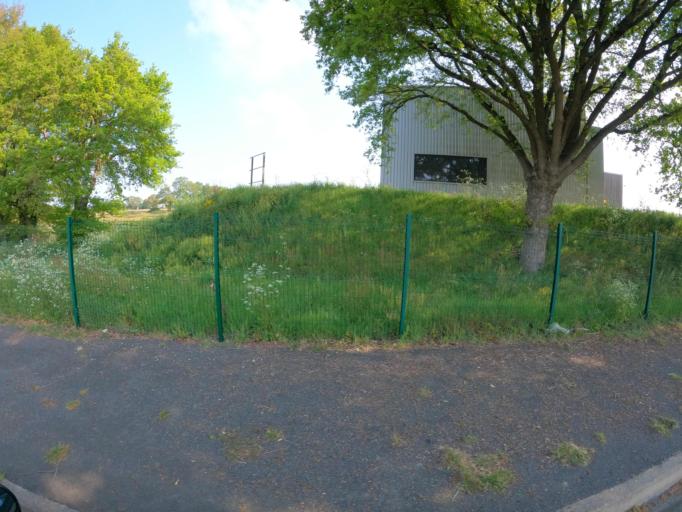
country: FR
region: Pays de la Loire
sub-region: Departement de Maine-et-Loire
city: La Romagne
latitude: 47.0605
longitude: -1.0096
